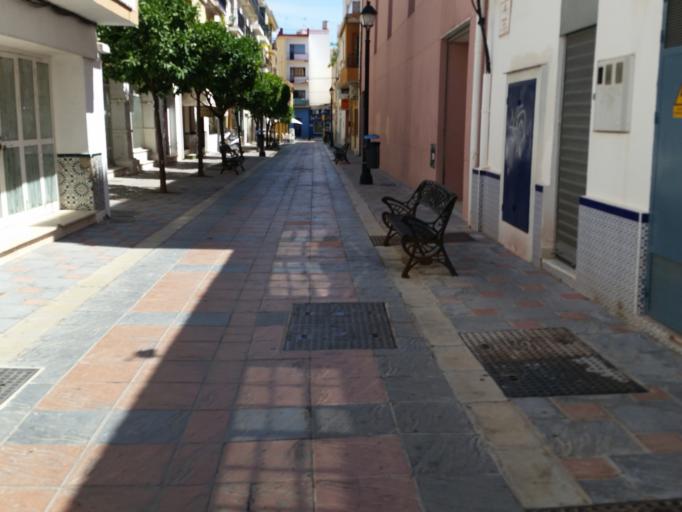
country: ES
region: Andalusia
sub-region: Provincia de Malaga
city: Fuengirola
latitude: 36.5386
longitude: -4.6253
